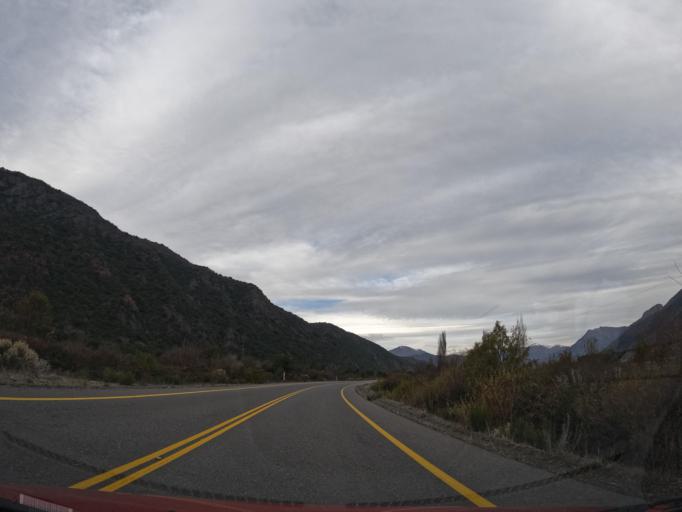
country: CL
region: Maule
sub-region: Provincia de Linares
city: Colbun
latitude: -35.7285
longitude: -71.0179
